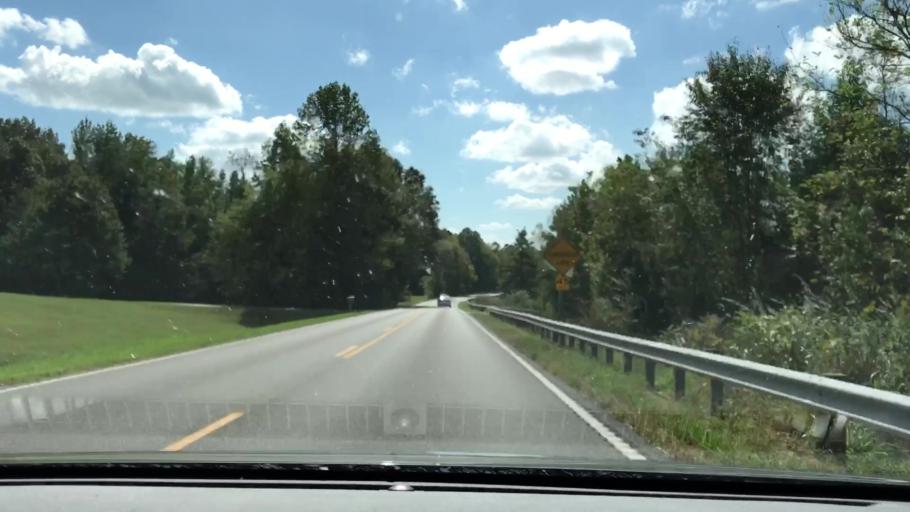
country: US
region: Kentucky
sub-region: McCracken County
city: Reidland
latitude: 36.9765
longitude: -88.5153
